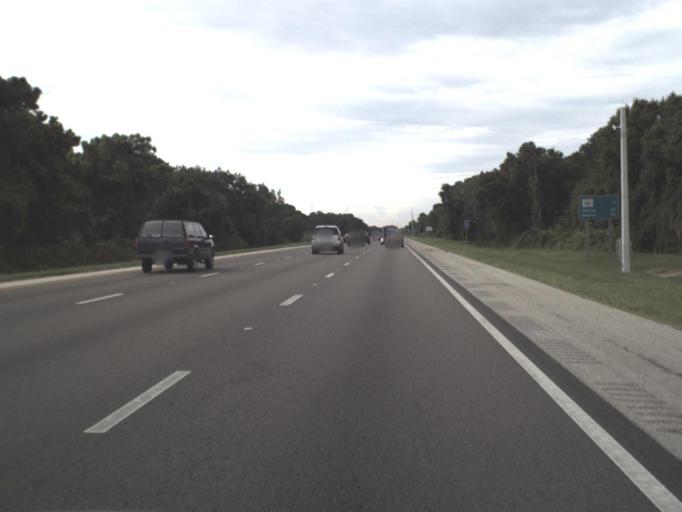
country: US
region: Florida
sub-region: Sarasota County
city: The Meadows
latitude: 27.3782
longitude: -82.4469
